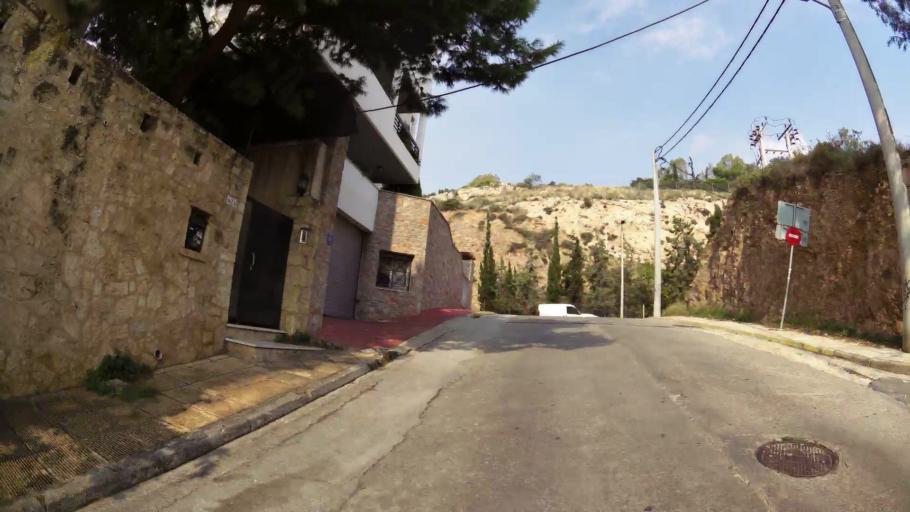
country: GR
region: Attica
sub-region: Nomarchia Athinas
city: Psychiko
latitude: 38.0035
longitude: 23.7627
